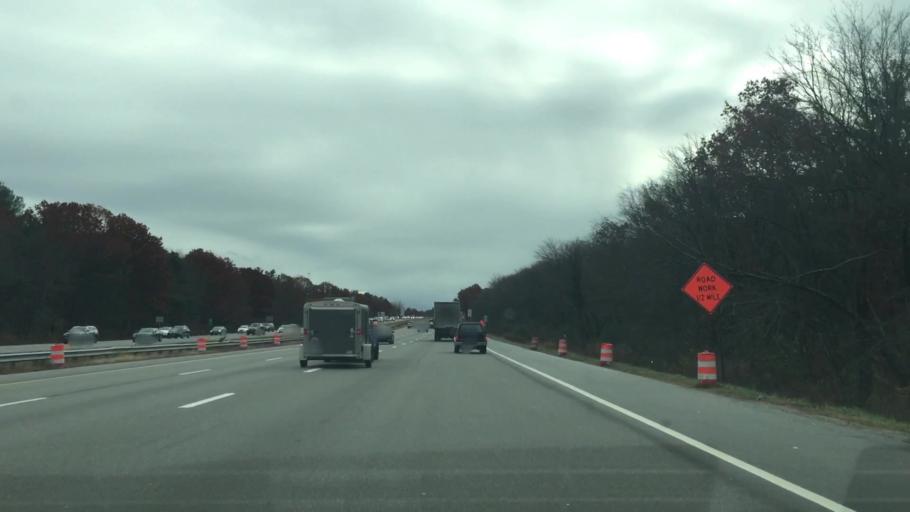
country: US
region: Massachusetts
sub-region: Essex County
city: Methuen
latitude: 42.7491
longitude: -71.2160
